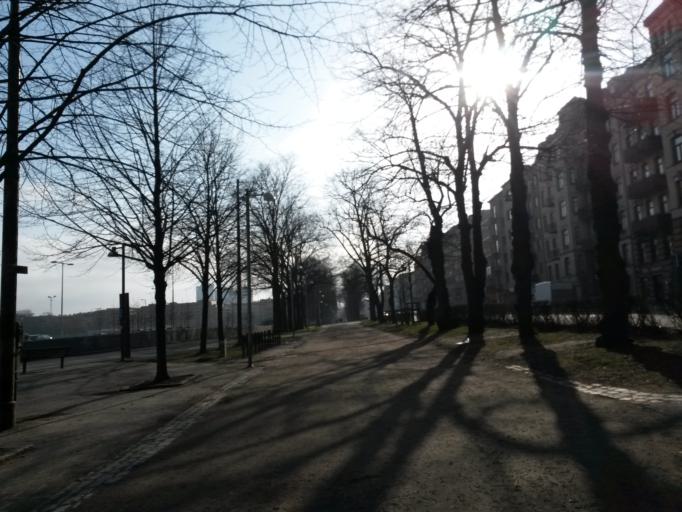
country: SE
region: Vaestra Goetaland
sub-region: Goteborg
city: Goeteborg
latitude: 57.7022
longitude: 11.9747
